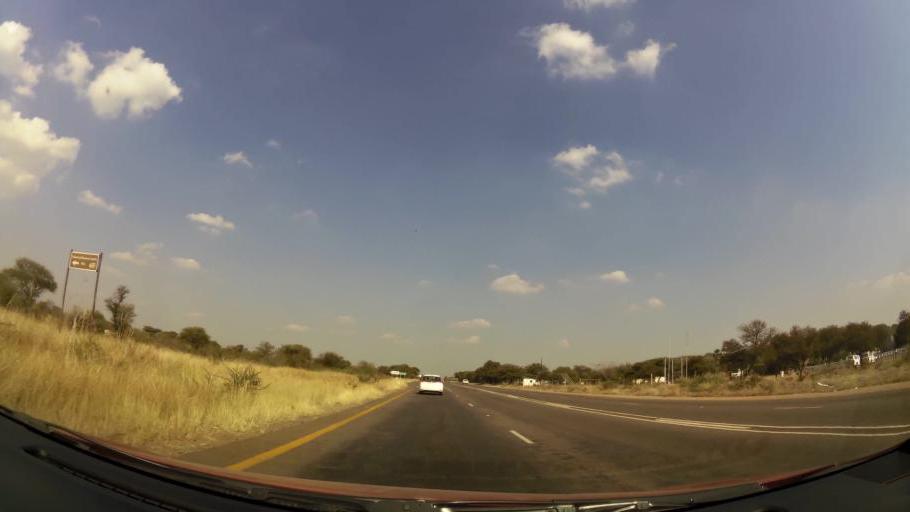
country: ZA
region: North-West
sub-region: Bojanala Platinum District Municipality
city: Mogwase
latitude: -25.4422
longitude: 27.0882
